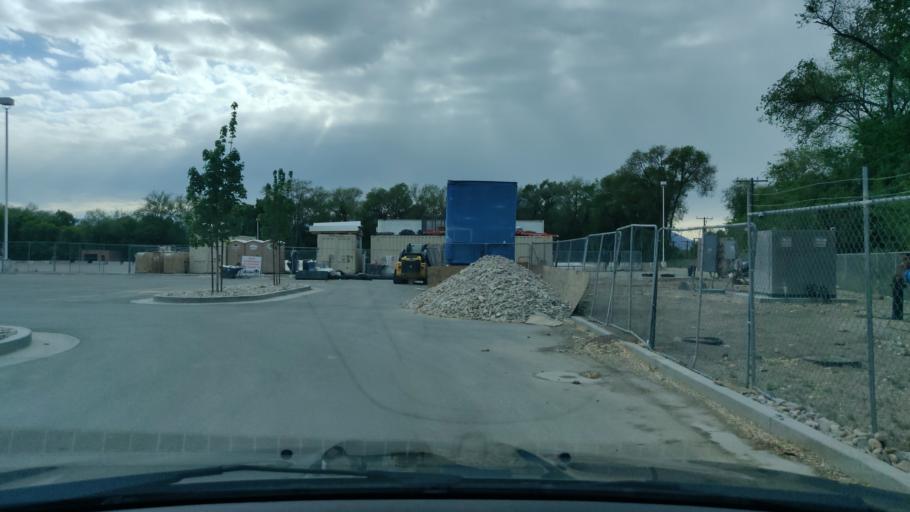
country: US
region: Utah
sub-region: Salt Lake County
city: Sandy City
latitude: 40.6200
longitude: -111.8685
